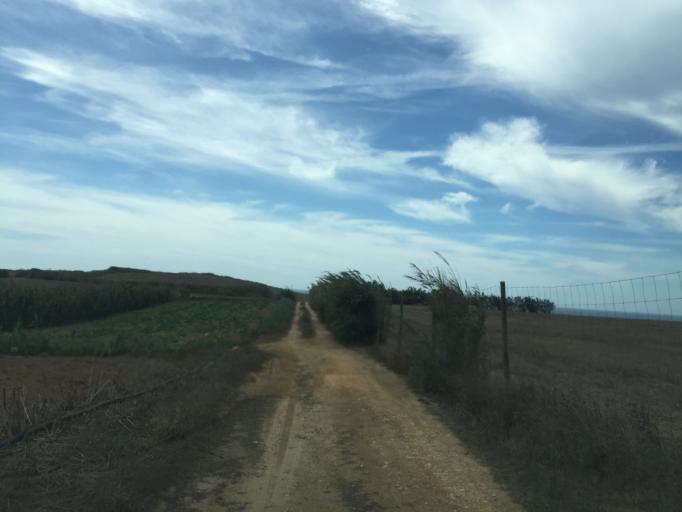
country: PT
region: Lisbon
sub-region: Lourinha
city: Lourinha
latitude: 39.1885
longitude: -9.3468
